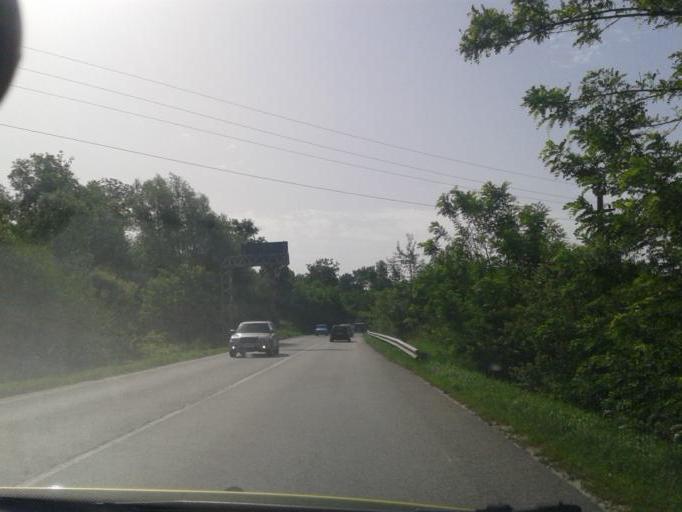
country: RO
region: Valcea
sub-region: Comuna Pietrari
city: Pietrari
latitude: 45.1009
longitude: 24.1241
